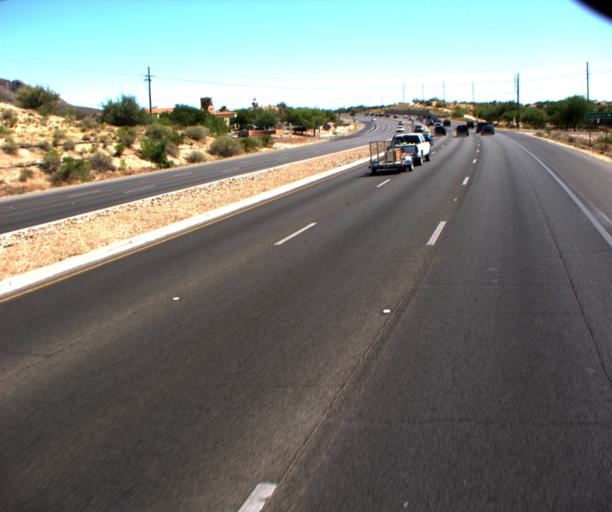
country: US
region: Arizona
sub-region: Pima County
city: Oro Valley
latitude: 32.3928
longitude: -110.9628
